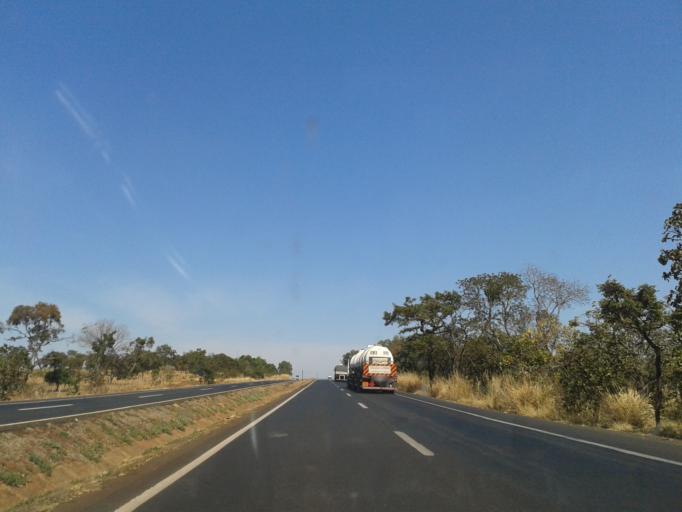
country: BR
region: Minas Gerais
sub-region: Monte Alegre De Minas
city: Monte Alegre de Minas
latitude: -18.8054
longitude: -49.0834
